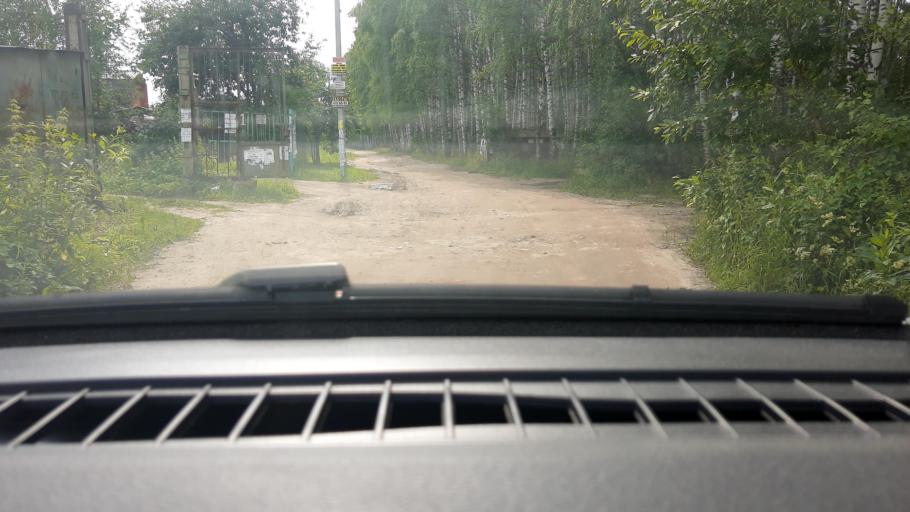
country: RU
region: Nizjnij Novgorod
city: Neklyudovo
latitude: 56.4294
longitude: 43.9947
